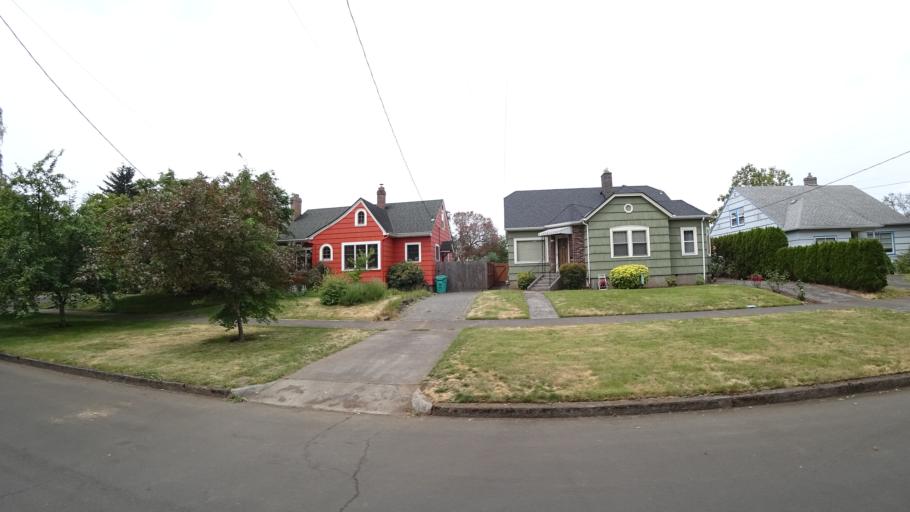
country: US
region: Oregon
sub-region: Multnomah County
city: Portland
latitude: 45.5642
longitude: -122.6915
